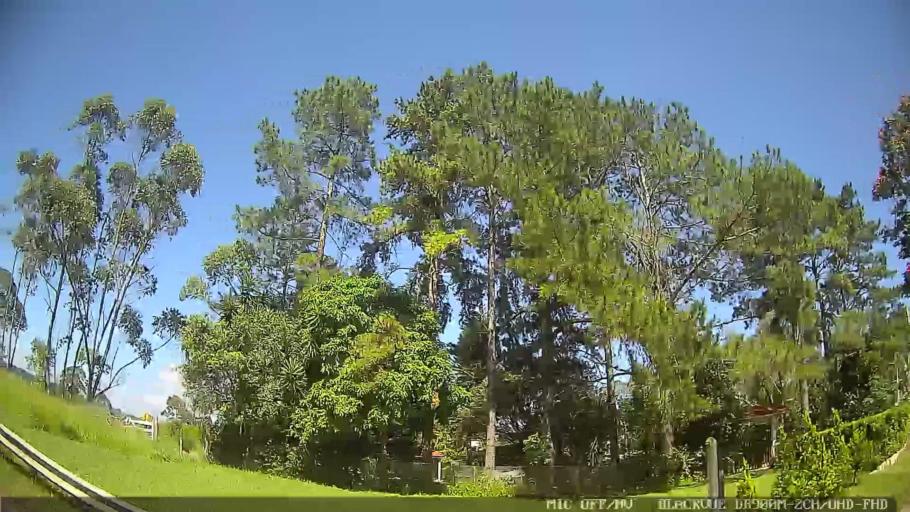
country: BR
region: Sao Paulo
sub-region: Suzano
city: Suzano
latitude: -23.6039
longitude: -46.2556
